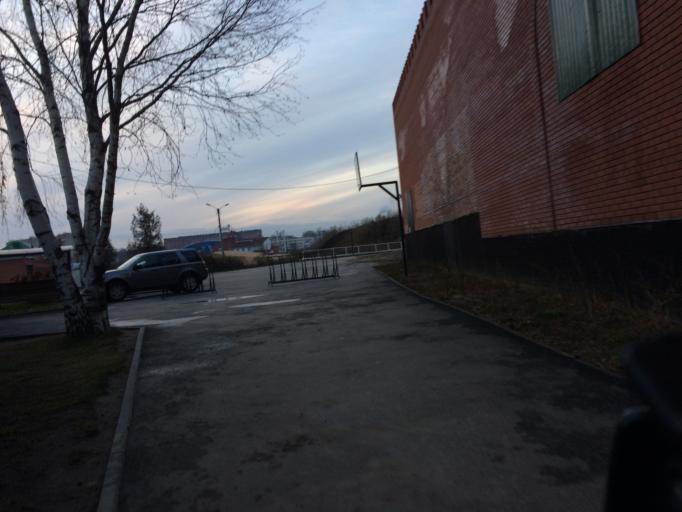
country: RU
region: Mariy-El
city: Yoshkar-Ola
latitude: 56.6265
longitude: 47.9036
